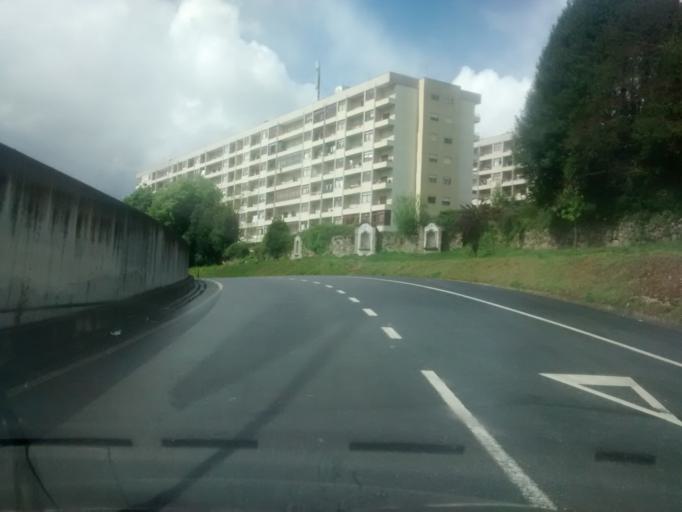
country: PT
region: Braga
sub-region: Braga
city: Braga
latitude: 41.5636
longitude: -8.4080
